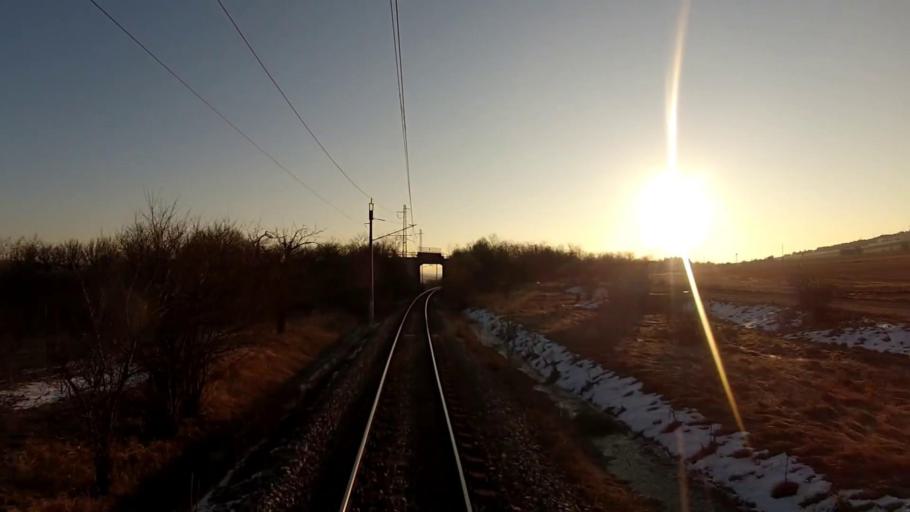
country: BG
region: Sofiya
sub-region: Obshtina Slivnitsa
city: Slivnitsa
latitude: 42.8774
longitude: 23.0170
